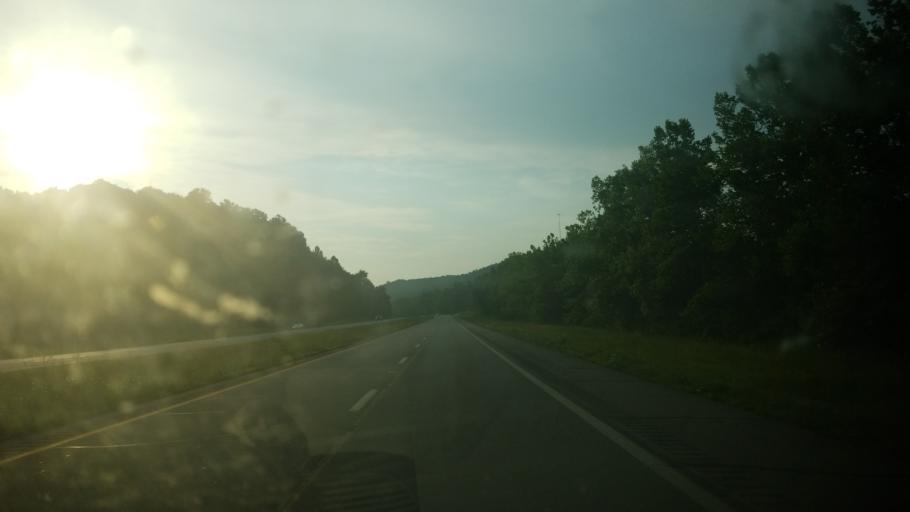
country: US
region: Ohio
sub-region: Pike County
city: Piketon
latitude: 39.0538
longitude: -83.0632
